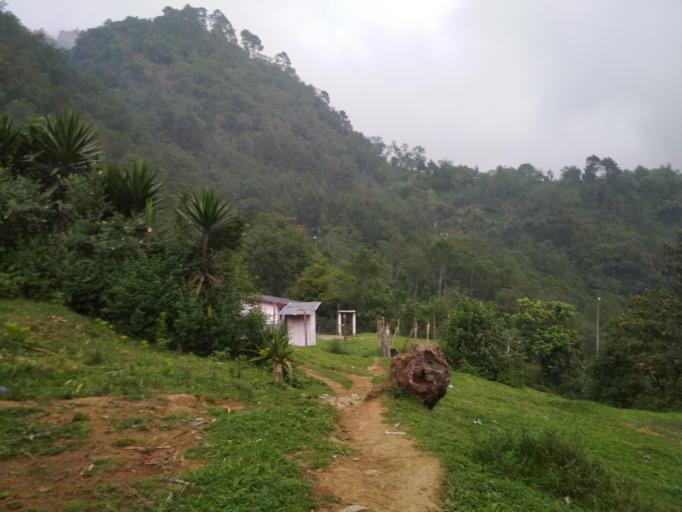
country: MX
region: Veracruz
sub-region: La Perla
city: Metlac Hernandez (Metlac Primero)
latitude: 18.9650
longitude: -97.1286
